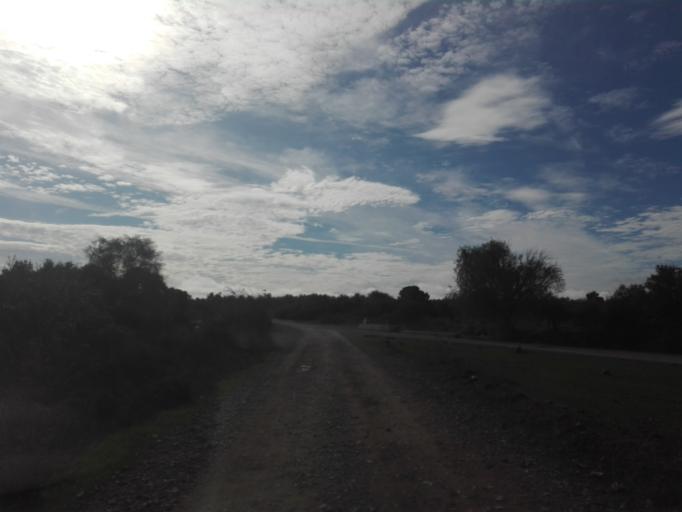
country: ES
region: Extremadura
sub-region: Provincia de Badajoz
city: Villagarcia de la Torre
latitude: 38.3013
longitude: -6.0868
